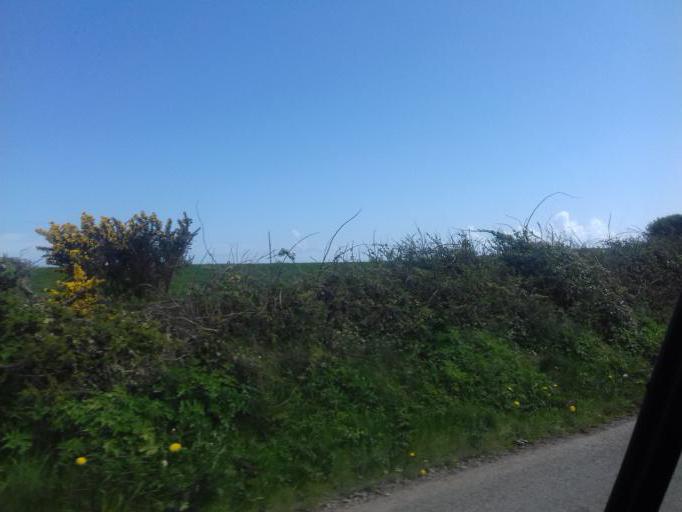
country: IE
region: Munster
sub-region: Waterford
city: Dunmore East
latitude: 52.1845
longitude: -6.8943
